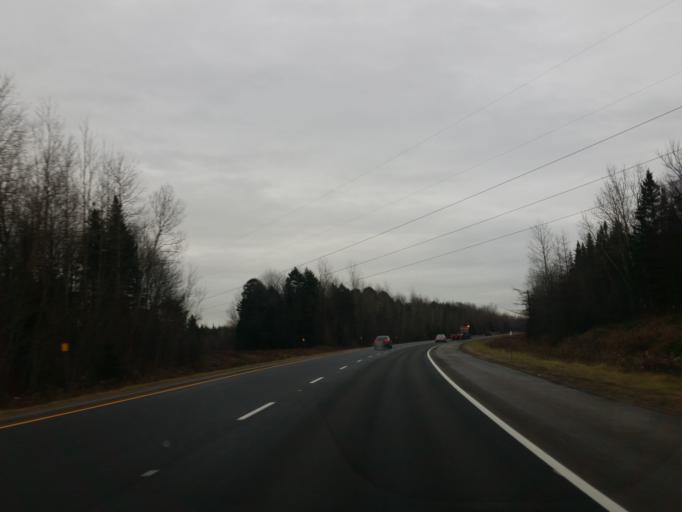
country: CA
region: Quebec
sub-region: Capitale-Nationale
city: Cap-Sante
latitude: 46.7029
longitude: -71.8450
